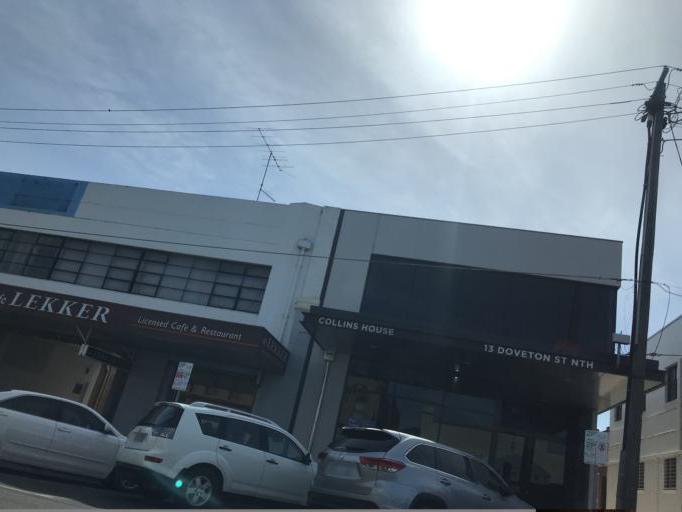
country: AU
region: Victoria
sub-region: Ballarat North
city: Ballarat Central
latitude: -37.5604
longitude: 143.8550
